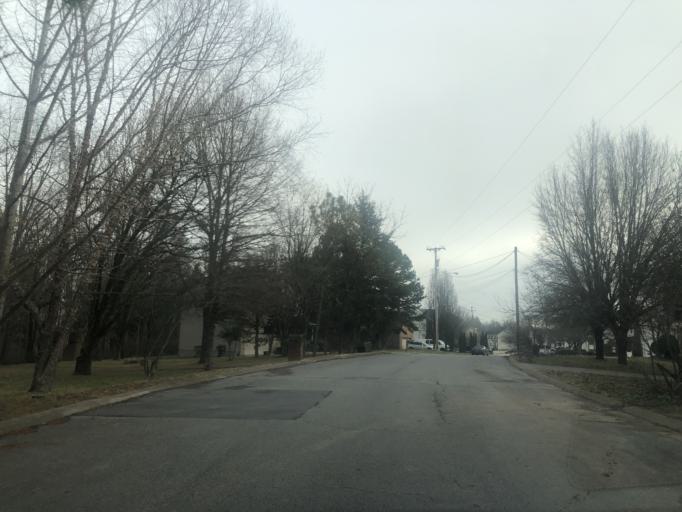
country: US
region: Tennessee
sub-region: Rutherford County
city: La Vergne
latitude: 36.0736
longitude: -86.6555
